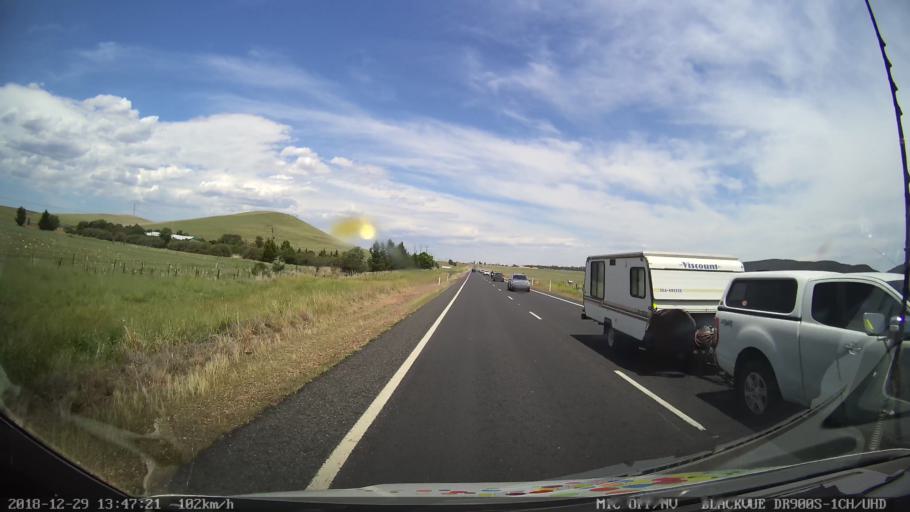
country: AU
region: New South Wales
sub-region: Cooma-Monaro
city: Cooma
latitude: -36.1254
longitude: 149.1425
